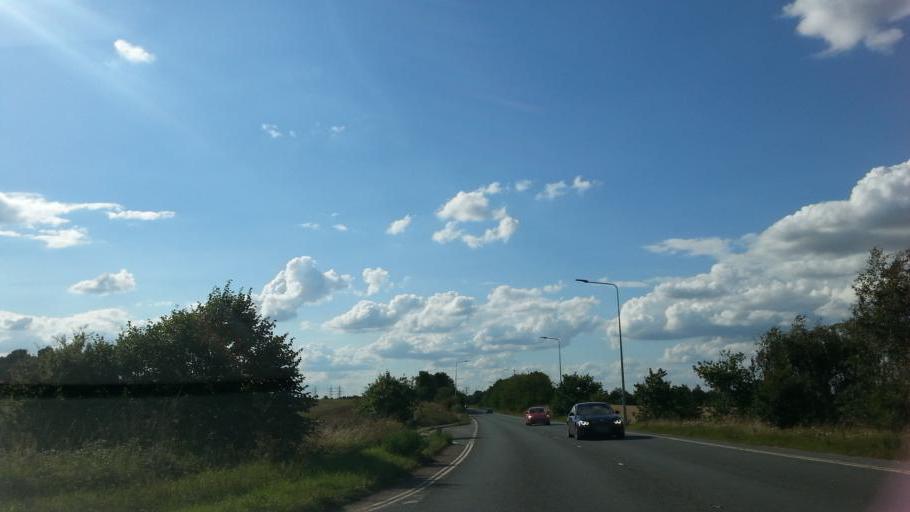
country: GB
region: England
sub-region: Suffolk
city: Bramford
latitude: 52.0474
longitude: 1.1057
